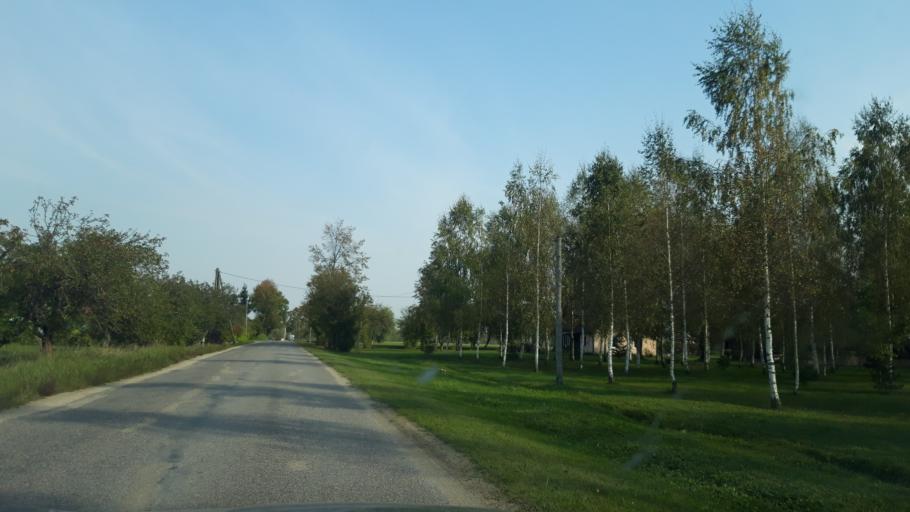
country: LV
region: Mazsalaca
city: Mazsalaca
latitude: 57.8531
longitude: 25.0376
